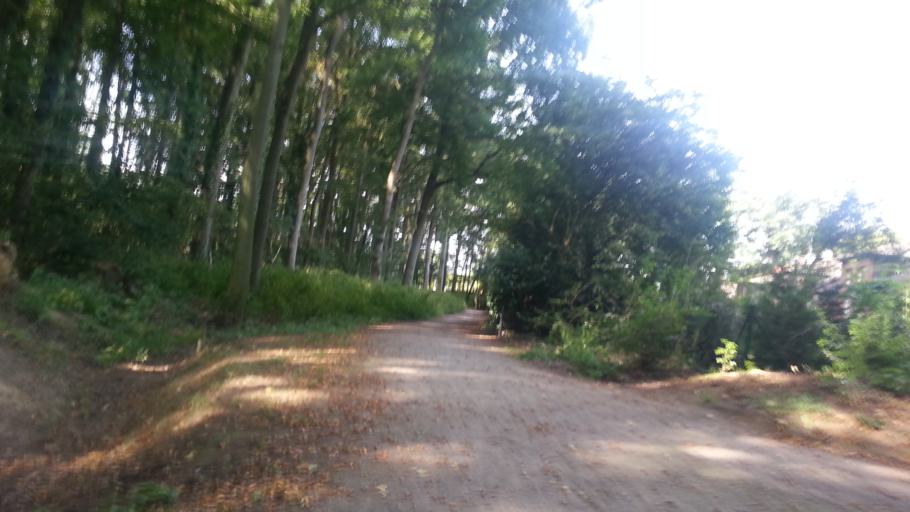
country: DE
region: North Rhine-Westphalia
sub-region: Regierungsbezirk Munster
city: Muenster
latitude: 51.9950
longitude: 7.5920
